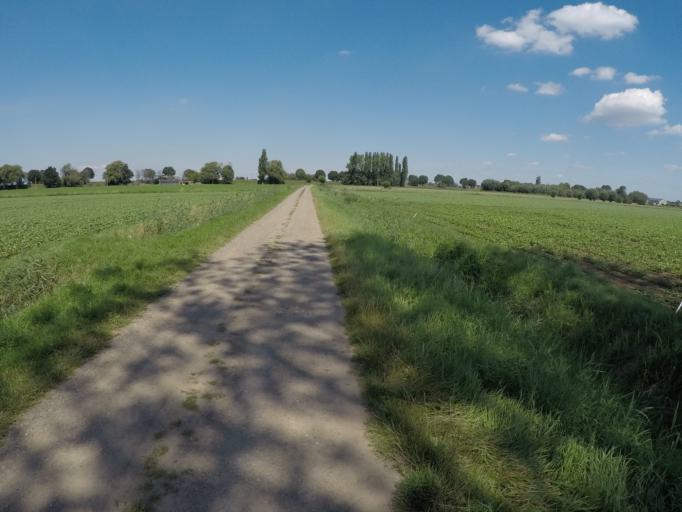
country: BE
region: Flanders
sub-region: Provincie Antwerpen
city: Stabroek
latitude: 51.3174
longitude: 4.3734
